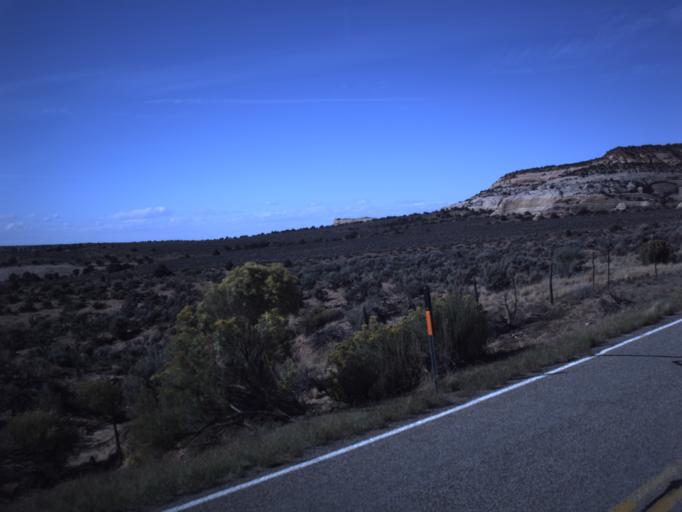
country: US
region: Utah
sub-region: San Juan County
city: Monticello
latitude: 38.0539
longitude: -109.4092
